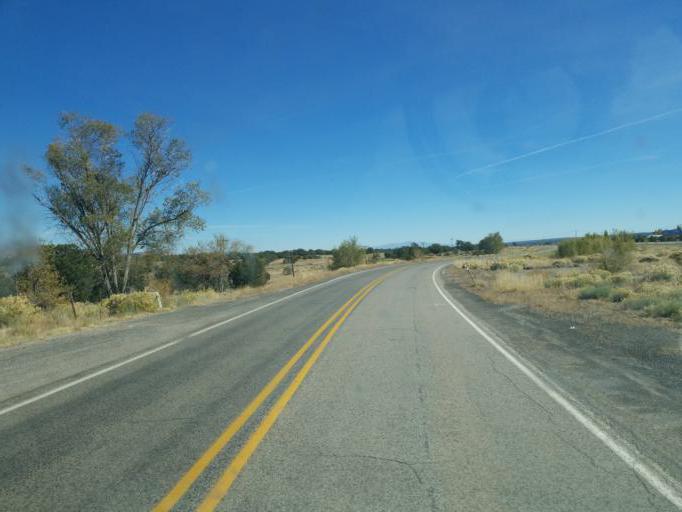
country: US
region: New Mexico
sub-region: McKinley County
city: Thoreau
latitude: 35.4222
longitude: -108.3077
